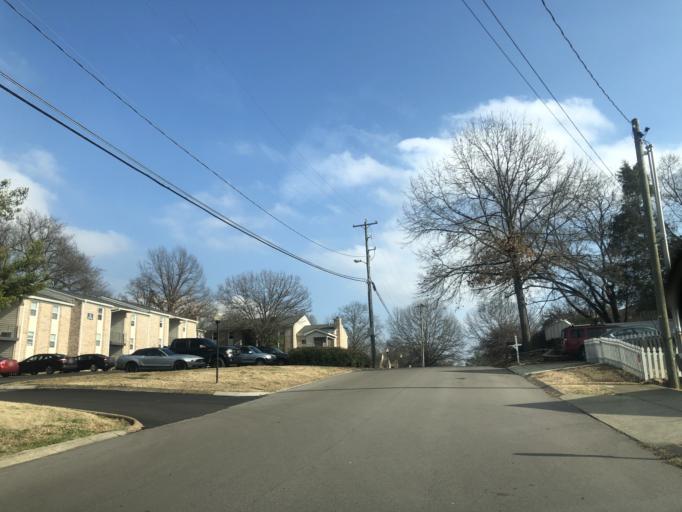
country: US
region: Tennessee
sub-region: Davidson County
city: Oak Hill
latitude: 36.1040
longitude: -86.7186
